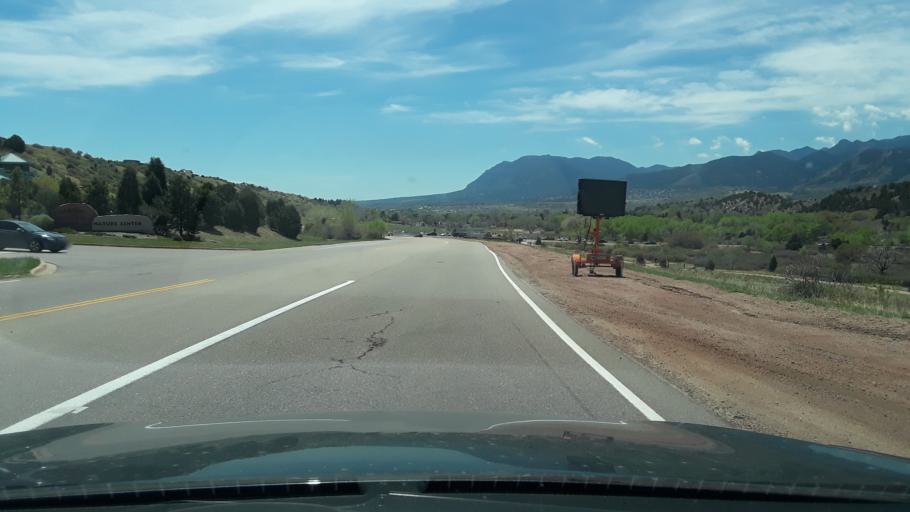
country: US
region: Colorado
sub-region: El Paso County
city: Manitou Springs
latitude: 38.8802
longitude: -104.8716
